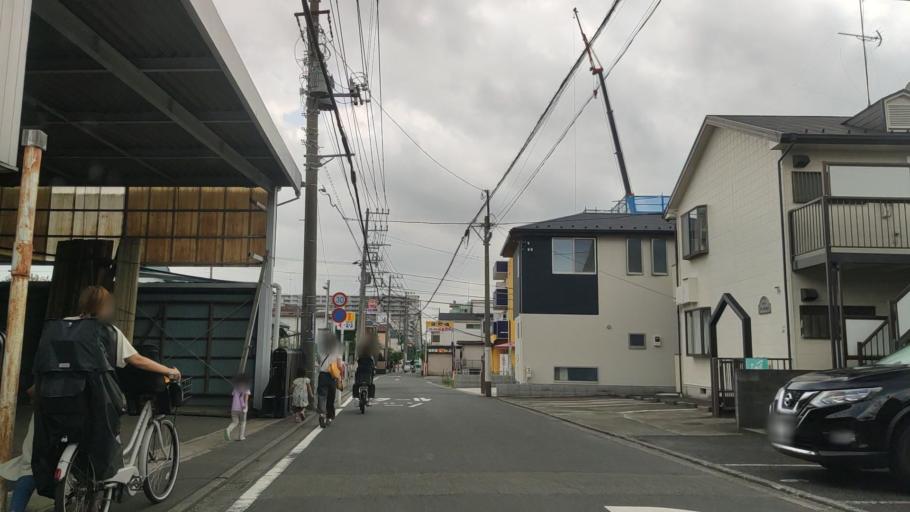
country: JP
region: Kanagawa
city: Minami-rinkan
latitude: 35.5107
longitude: 139.4480
